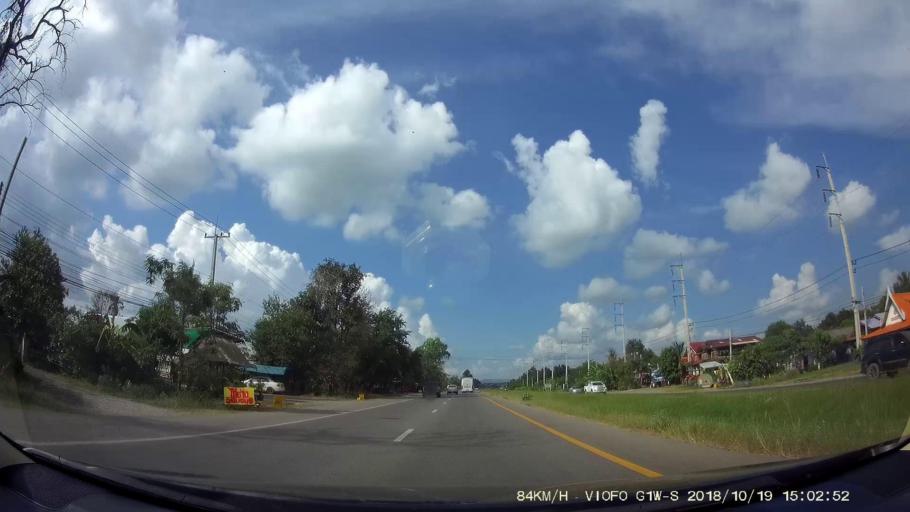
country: TH
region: Chaiyaphum
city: Phu Khiao
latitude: 16.4043
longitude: 102.1313
